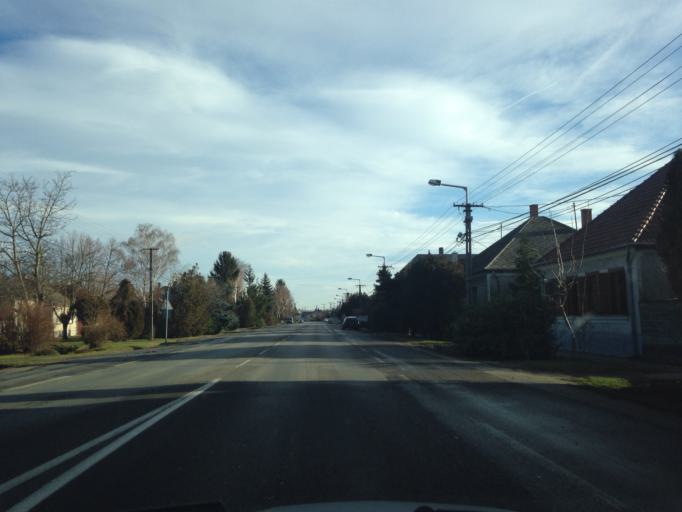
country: HU
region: Gyor-Moson-Sopron
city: Otteveny
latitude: 47.7235
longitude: 17.4943
